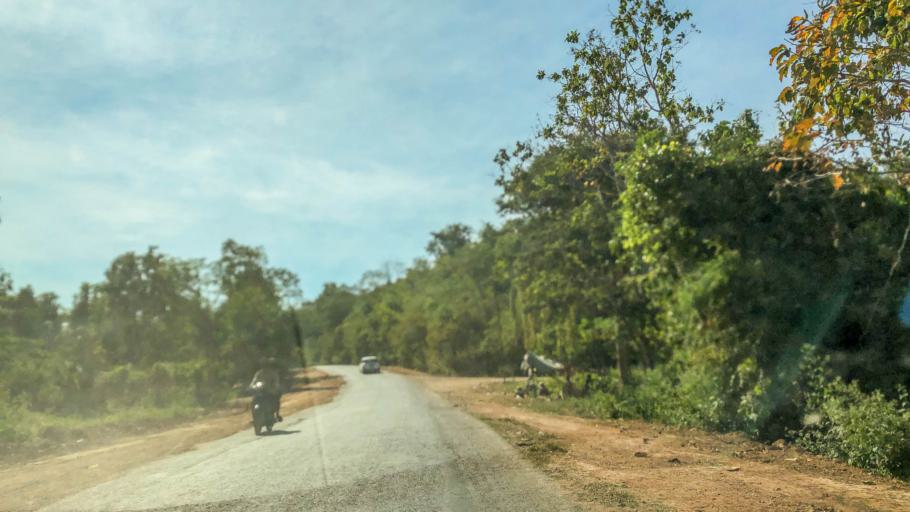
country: MM
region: Magway
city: Magway
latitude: 19.7641
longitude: 94.9379
